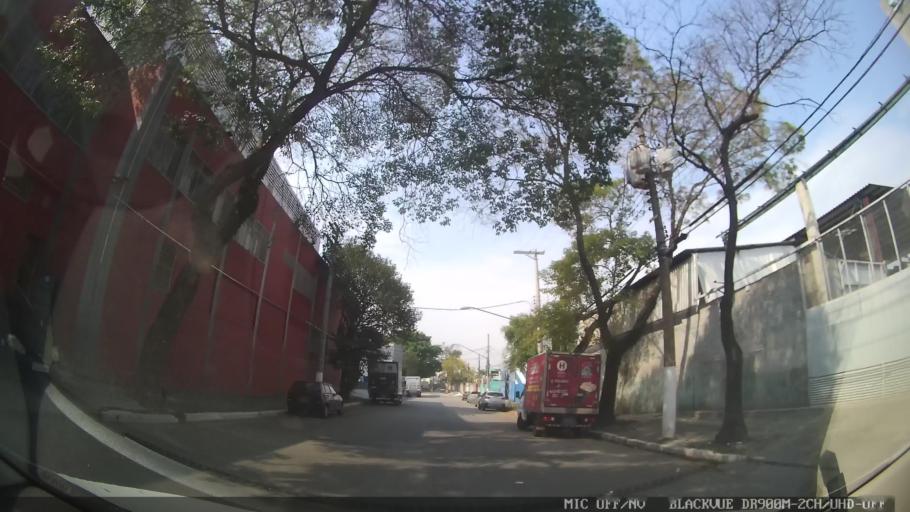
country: BR
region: Sao Paulo
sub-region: Sao Caetano Do Sul
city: Sao Caetano do Sul
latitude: -23.5886
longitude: -46.5964
